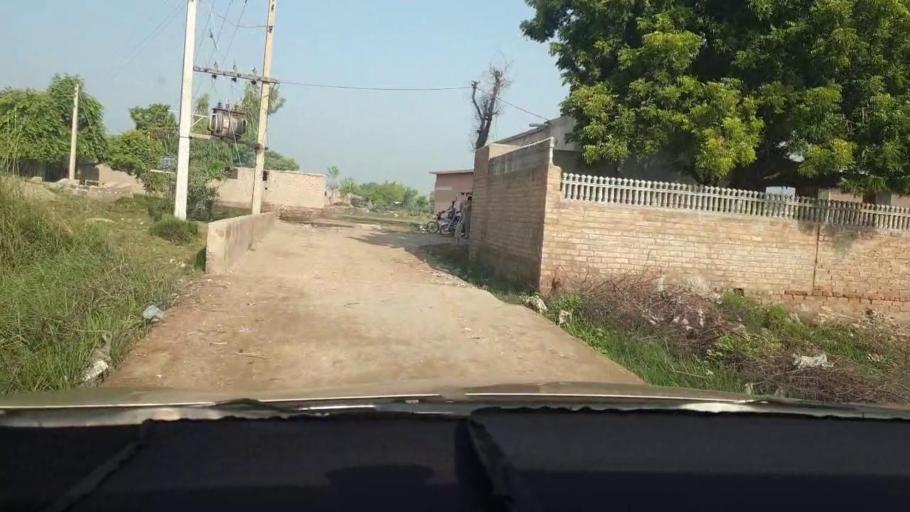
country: PK
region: Sindh
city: Larkana
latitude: 27.6038
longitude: 68.1135
